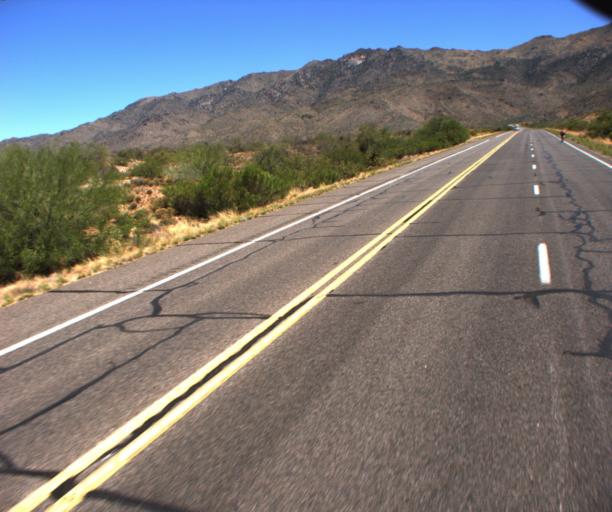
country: US
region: Arizona
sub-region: Yavapai County
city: Congress
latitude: 34.1963
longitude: -112.8119
